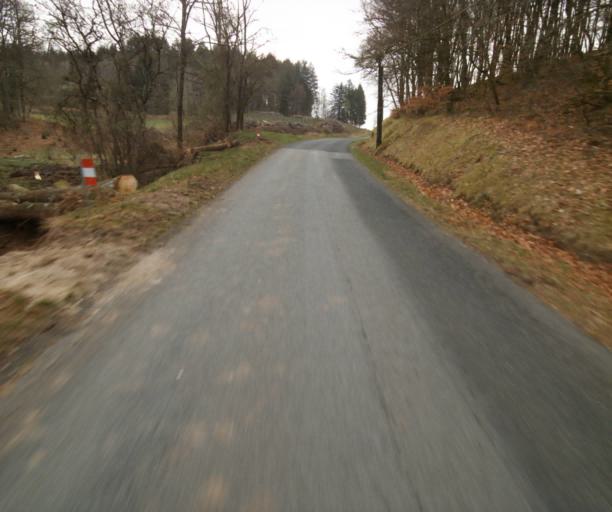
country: FR
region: Limousin
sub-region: Departement de la Correze
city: Correze
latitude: 45.4240
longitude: 1.8638
